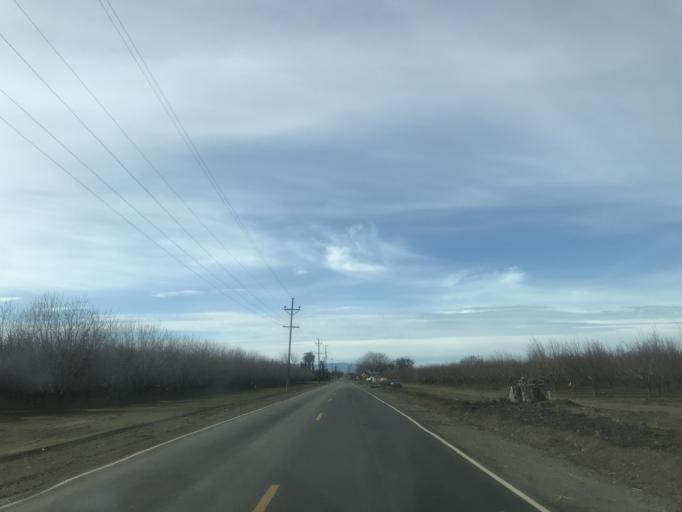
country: US
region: California
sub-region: Yolo County
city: Woodland
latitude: 38.6634
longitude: -121.8314
